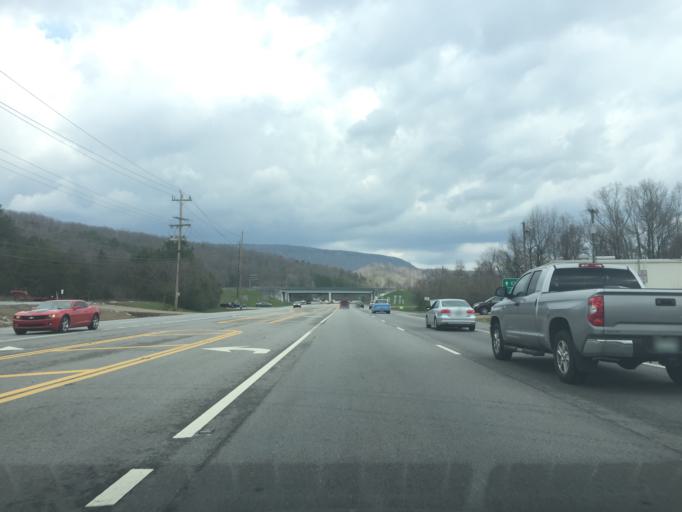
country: US
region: Tennessee
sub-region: Hamilton County
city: Falling Water
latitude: 35.1853
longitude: -85.2464
